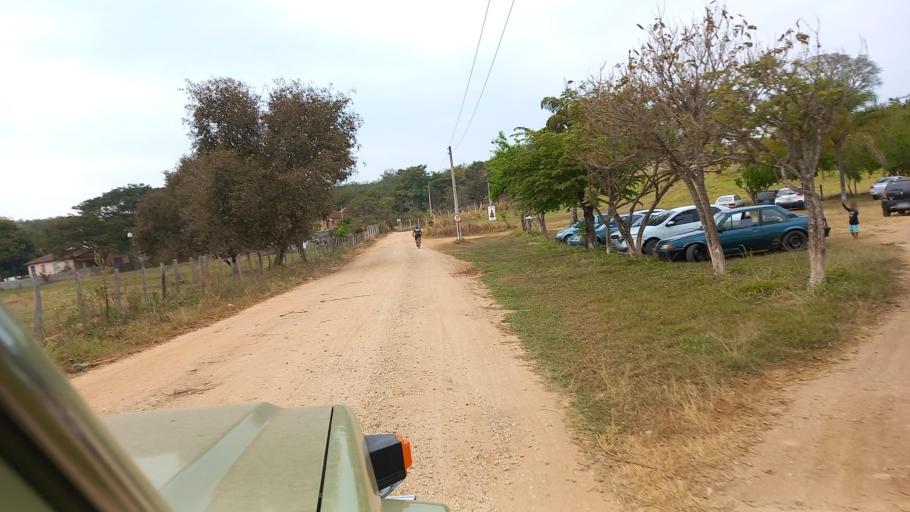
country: BR
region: Sao Paulo
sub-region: Moji-Guacu
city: Mogi-Gaucu
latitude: -22.2748
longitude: -46.8461
